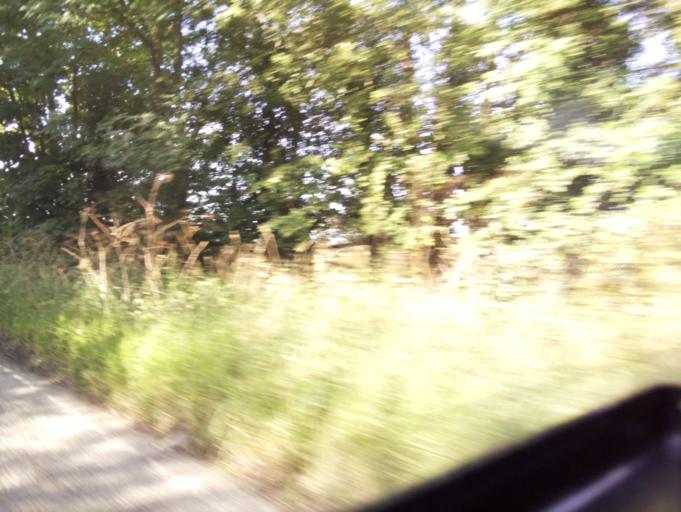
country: GB
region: England
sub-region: South Gloucestershire
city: Pucklechurch
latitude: 51.4426
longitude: -2.4152
